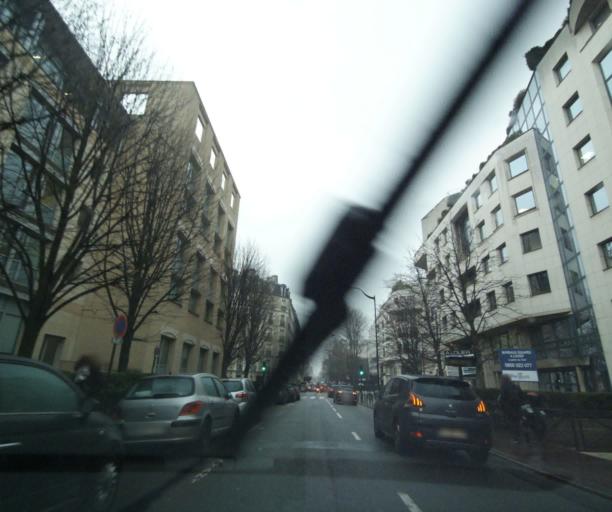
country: FR
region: Ile-de-France
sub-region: Departement des Hauts-de-Seine
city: Levallois-Perret
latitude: 48.8943
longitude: 2.2831
